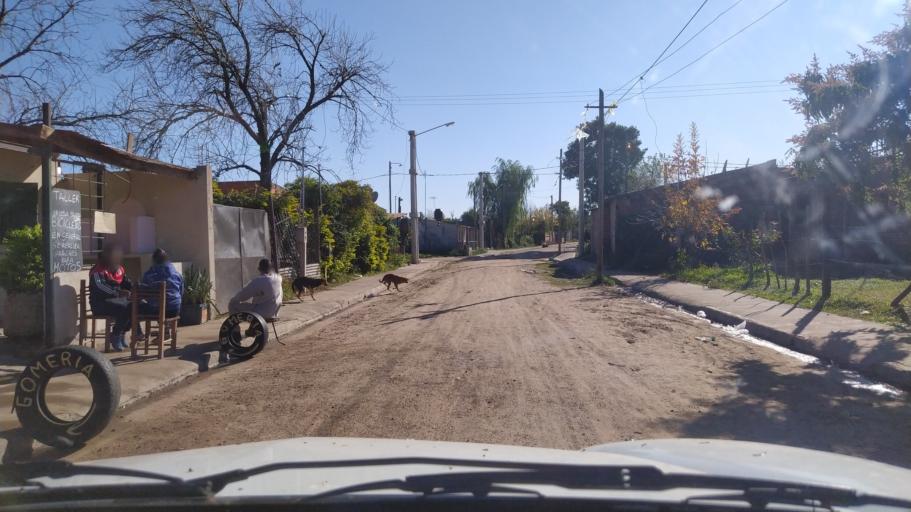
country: AR
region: Corrientes
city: Corrientes
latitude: -27.4988
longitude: -58.8058
